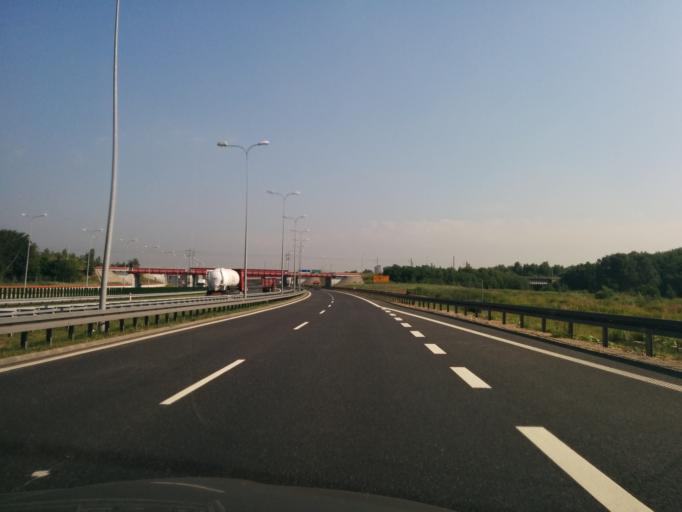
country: PL
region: Silesian Voivodeship
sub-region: Powiat gliwicki
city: Przyszowice
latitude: 50.2718
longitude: 18.7297
